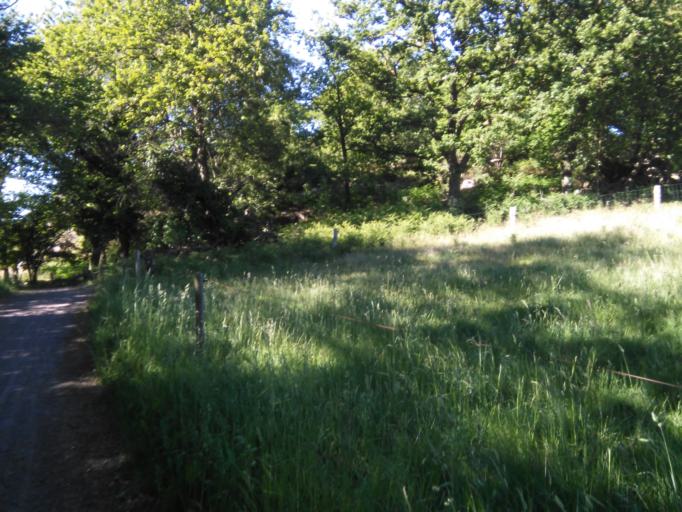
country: DK
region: Capital Region
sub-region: Bornholm Kommune
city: Ronne
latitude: 55.2590
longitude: 14.7701
